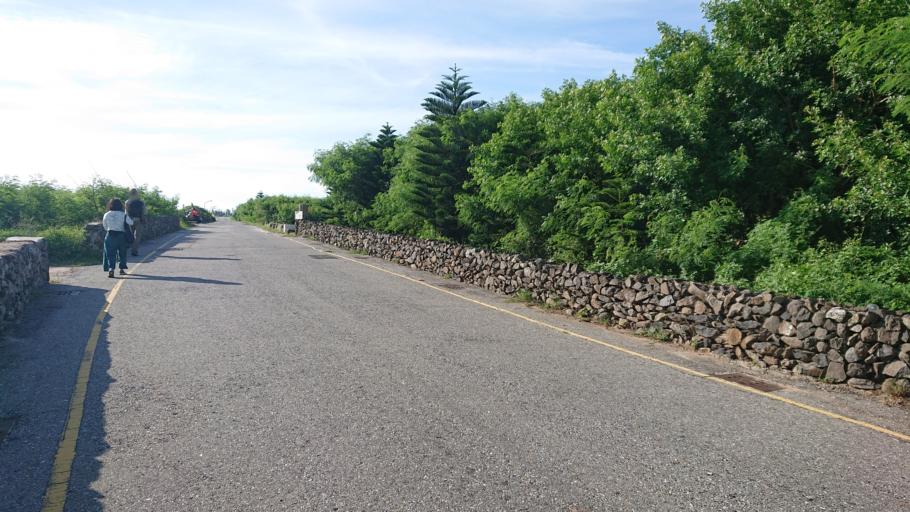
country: TW
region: Taiwan
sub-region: Penghu
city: Ma-kung
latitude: 23.6062
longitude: 119.5192
